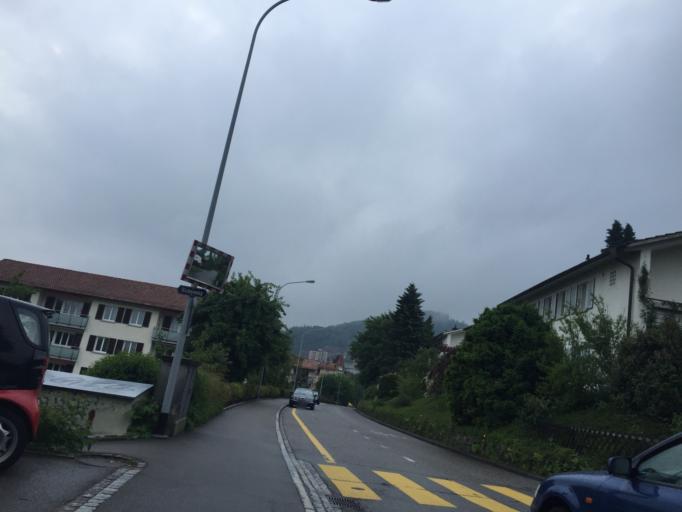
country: CH
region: Saint Gallen
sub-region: Wahlkreis St. Gallen
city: Sankt Gallen
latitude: 47.4066
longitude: 9.3314
